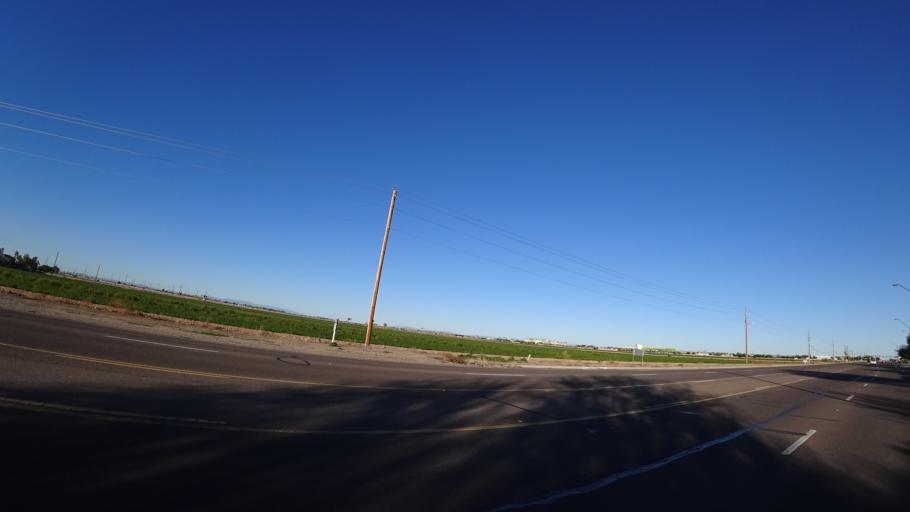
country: US
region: Arizona
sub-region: Maricopa County
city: Avondale
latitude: 33.4498
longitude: -112.3143
